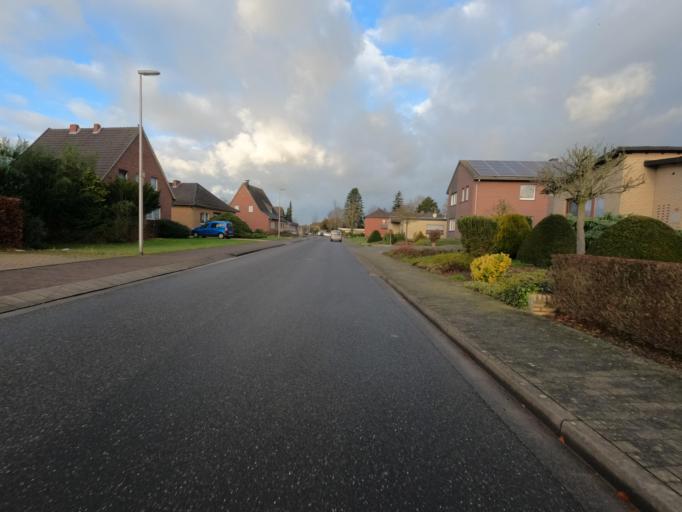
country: NL
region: Limburg
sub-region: Gemeente Roerdalen
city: Vlodrop
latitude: 51.0997
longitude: 6.0853
